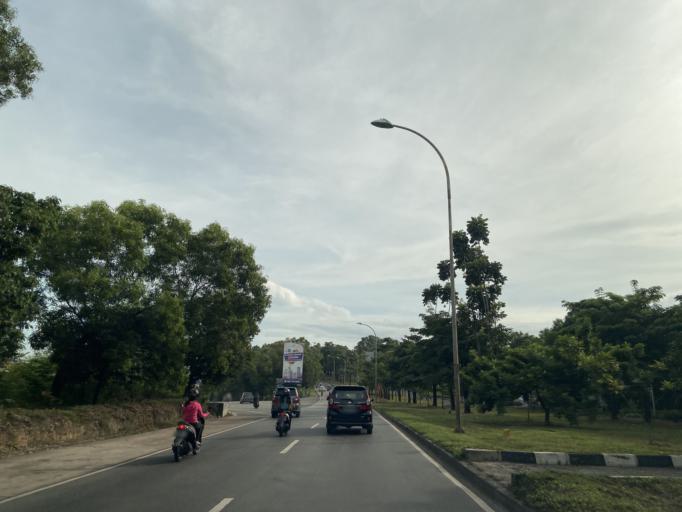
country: SG
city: Singapore
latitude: 1.1385
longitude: 104.0231
